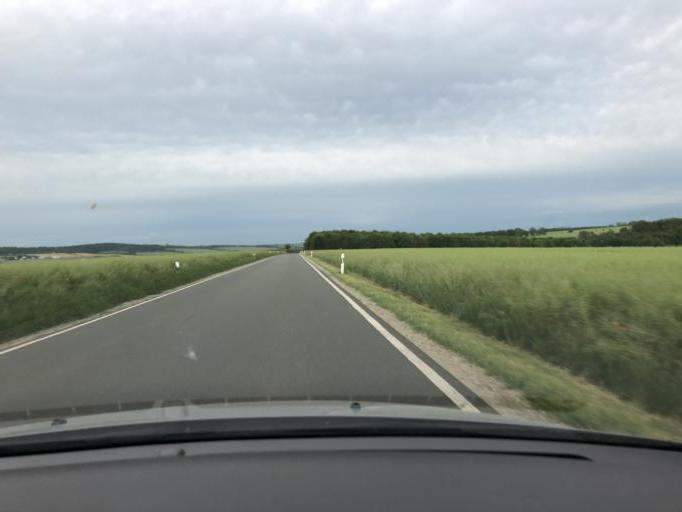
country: DE
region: Thuringia
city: Kodderitzsch
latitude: 51.0975
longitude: 11.5124
